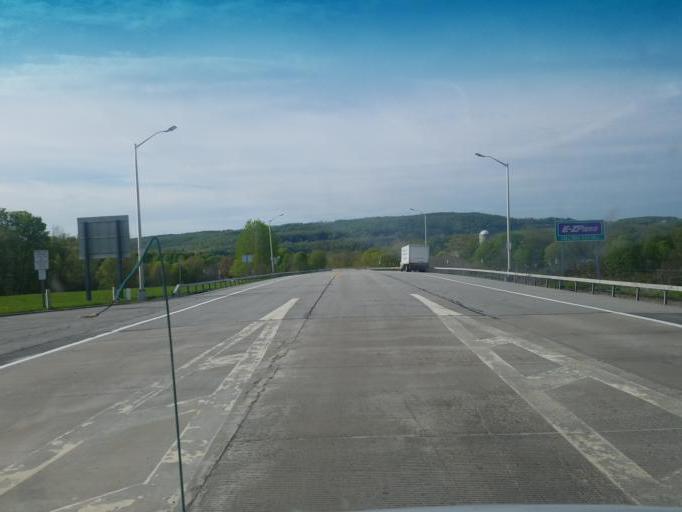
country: US
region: New York
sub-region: Herkimer County
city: Little Falls
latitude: 43.0194
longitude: -74.8184
